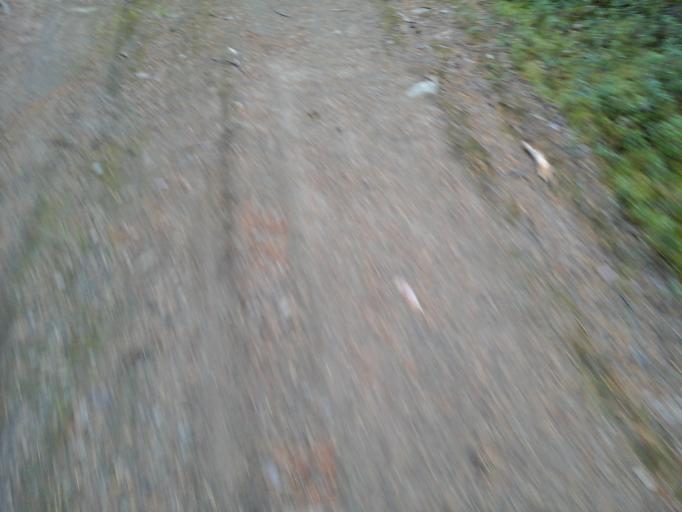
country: RU
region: Murmansk
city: Apatity
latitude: 67.5233
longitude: 33.2554
